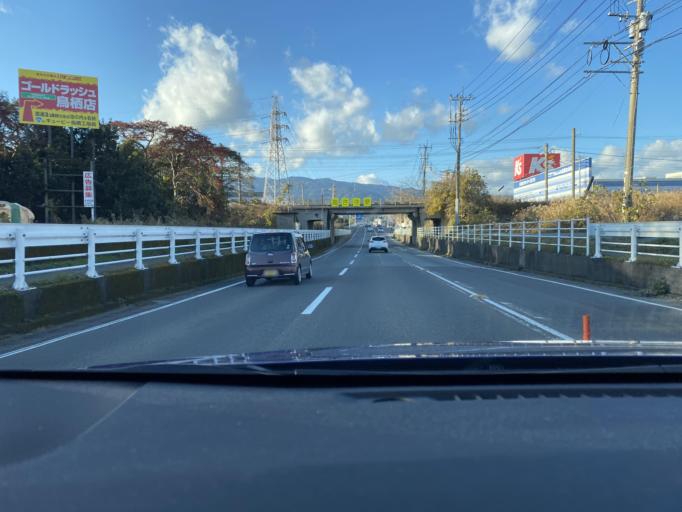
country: JP
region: Saga Prefecture
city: Tosu
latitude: 33.3616
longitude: 130.5052
